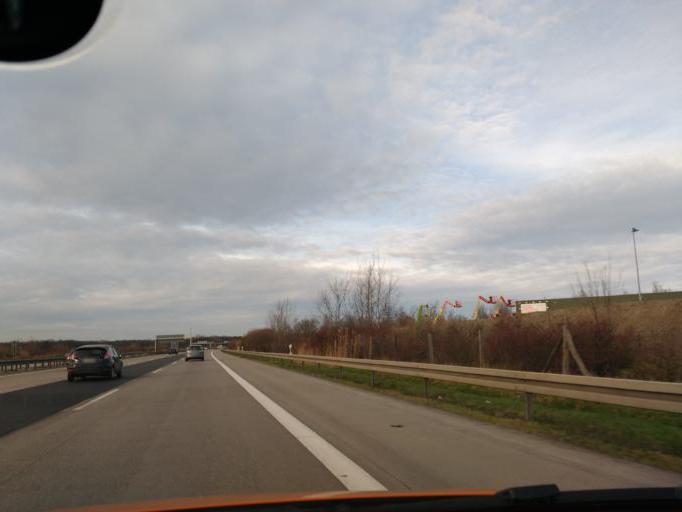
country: DE
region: Lower Saxony
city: Isernhagen Farster Bauerschaft
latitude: 52.4419
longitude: 9.8711
